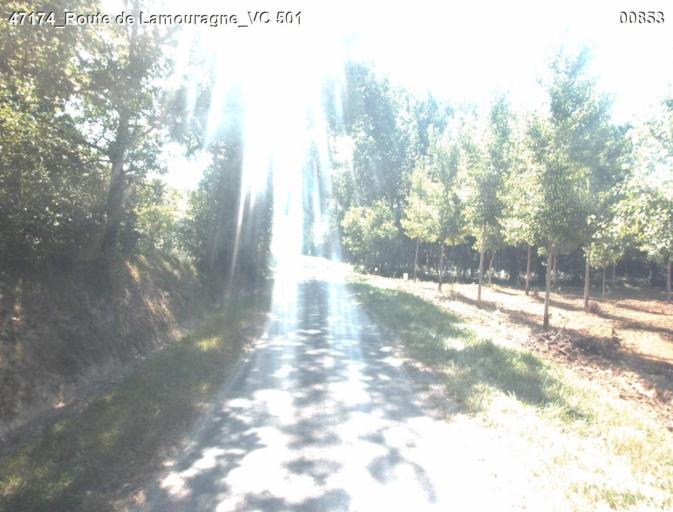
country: FR
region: Midi-Pyrenees
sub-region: Departement du Gers
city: Condom
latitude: 44.0401
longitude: 0.3870
